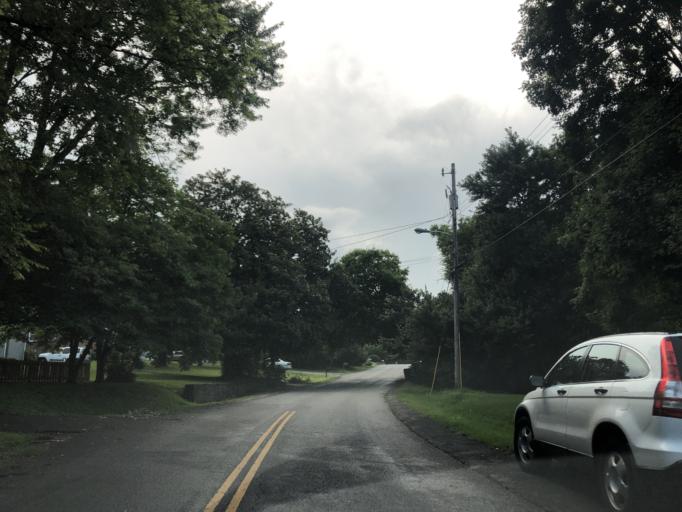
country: US
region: Tennessee
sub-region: Davidson County
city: Lakewood
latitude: 36.1780
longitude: -86.6808
